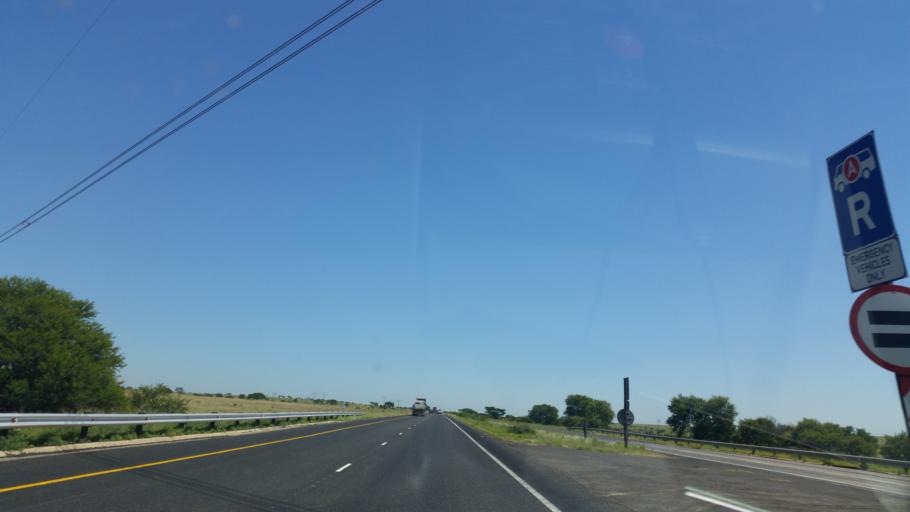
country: ZA
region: KwaZulu-Natal
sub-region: uThukela District Municipality
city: Ladysmith
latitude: -28.6597
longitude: 29.6298
